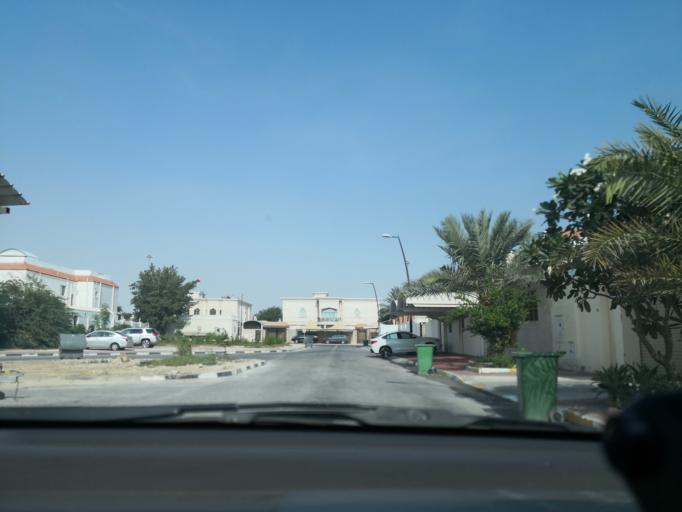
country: QA
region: Baladiyat ad Dawhah
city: Doha
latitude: 25.3468
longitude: 51.4901
